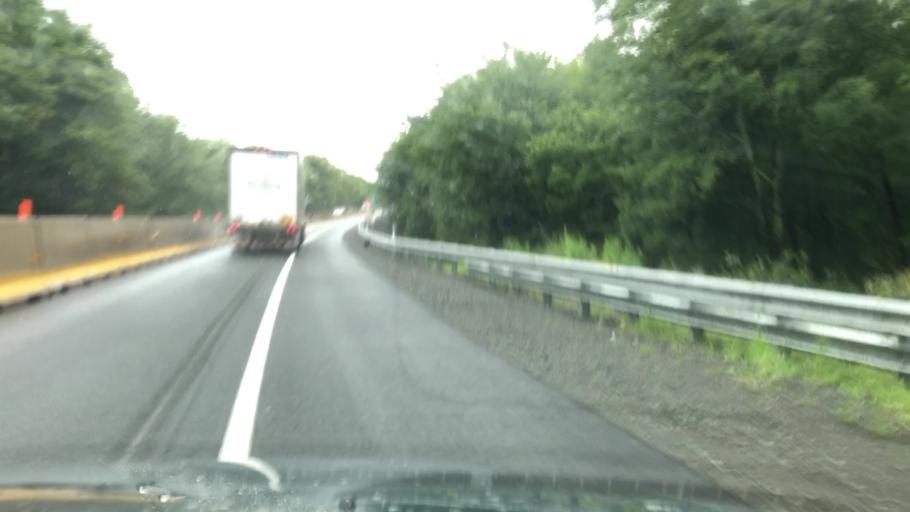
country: US
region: Pennsylvania
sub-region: Pike County
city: Hemlock Farms
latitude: 41.3532
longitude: -75.0346
